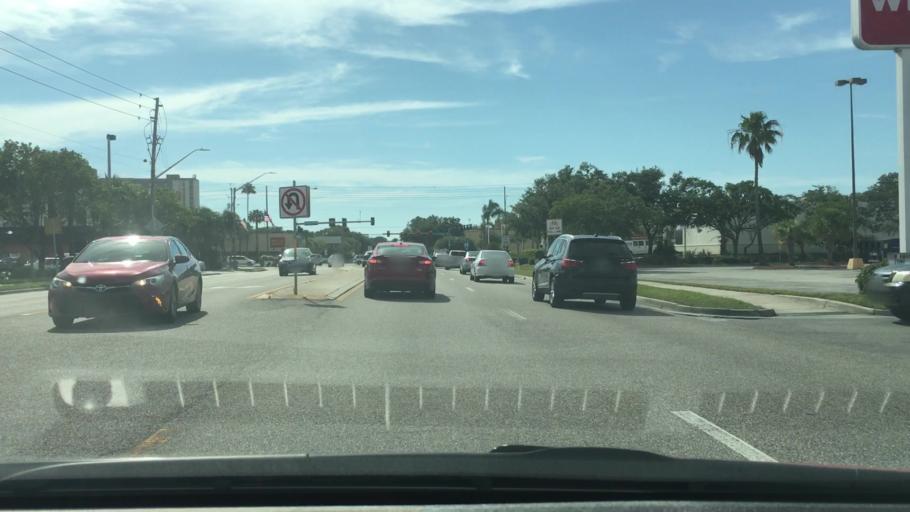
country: US
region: Florida
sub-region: Pinellas County
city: South Pasadena
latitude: 27.7587
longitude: -82.7344
